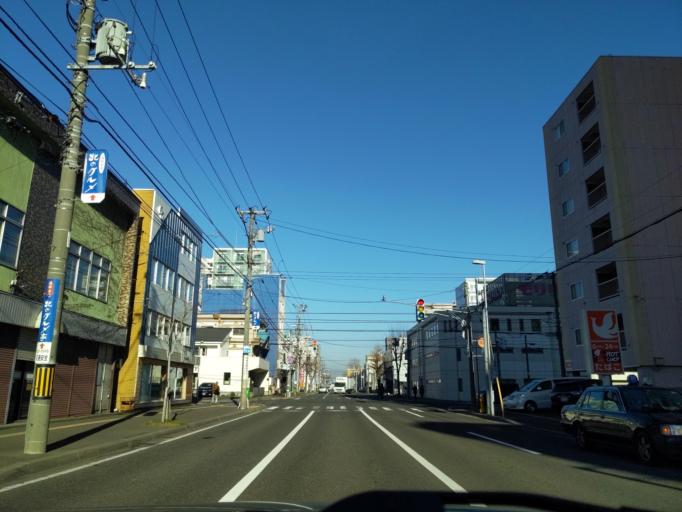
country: JP
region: Hokkaido
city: Sapporo
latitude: 43.0652
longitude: 141.3251
